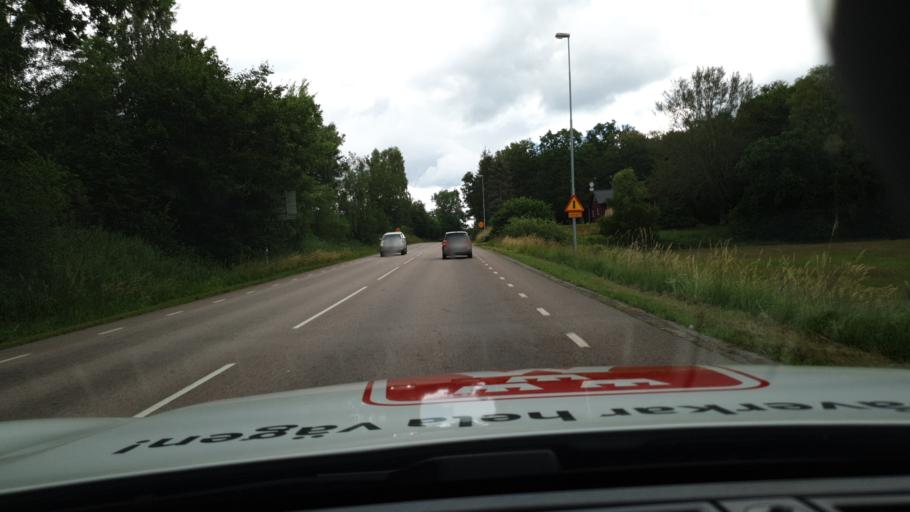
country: SE
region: Skane
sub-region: Hassleholms Kommun
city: Tormestorp
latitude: 56.1397
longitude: 13.7393
